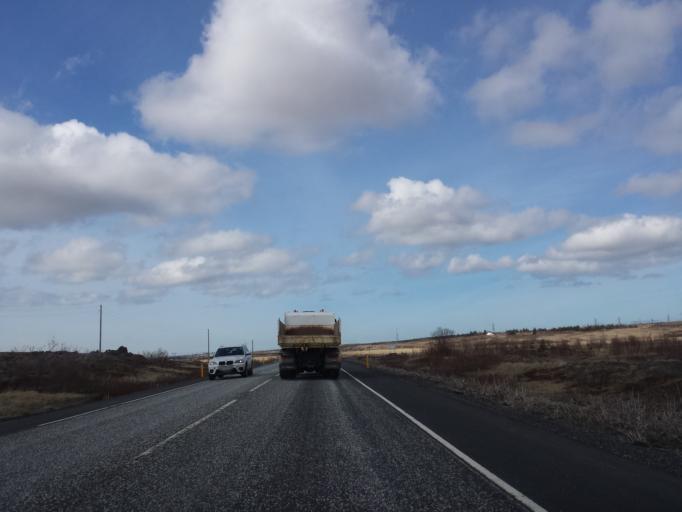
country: IS
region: Capital Region
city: Mosfellsbaer
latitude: 64.0834
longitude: -21.6774
